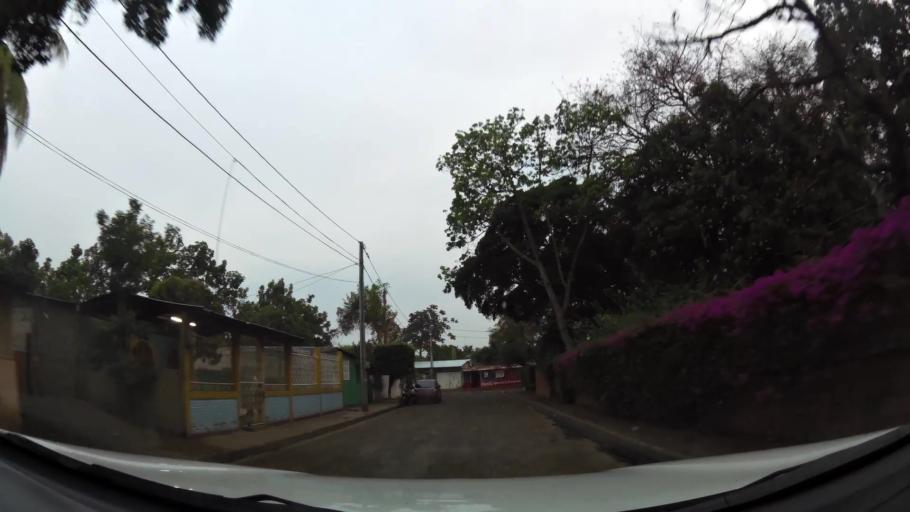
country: NI
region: Masaya
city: Nindiri
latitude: 12.0007
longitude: -86.1190
